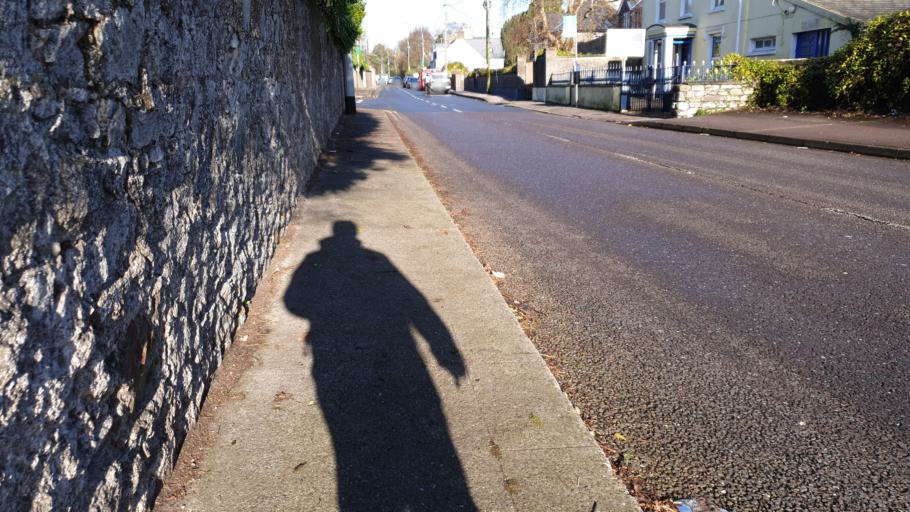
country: IE
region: Munster
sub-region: County Cork
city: Cork
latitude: 51.8942
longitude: -8.4202
